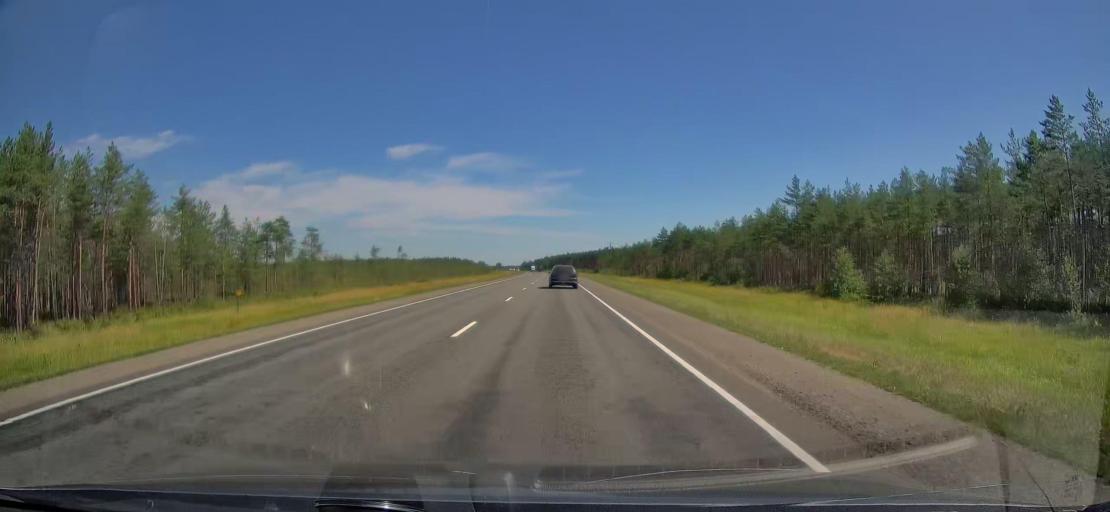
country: RU
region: Vologda
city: Khokhlovo
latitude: 58.9288
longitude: 37.2560
